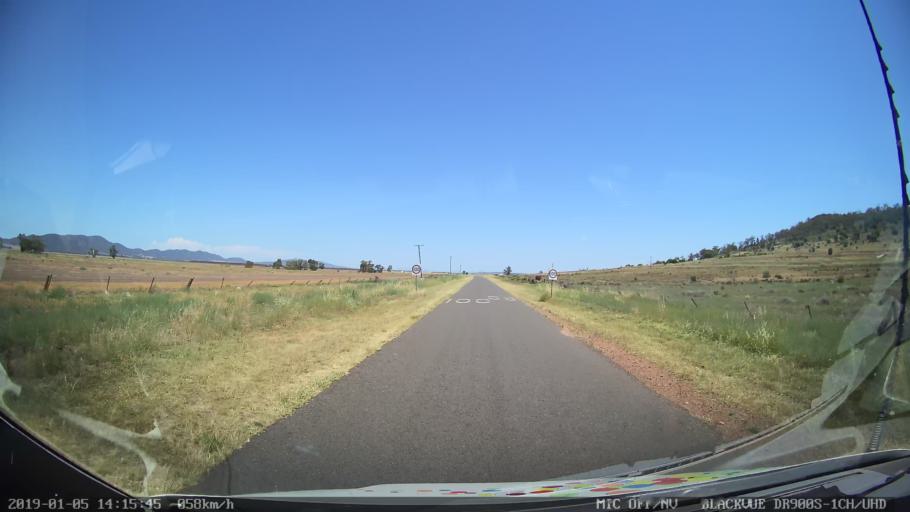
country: AU
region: New South Wales
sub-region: Liverpool Plains
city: Quirindi
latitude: -31.2498
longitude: 150.4714
